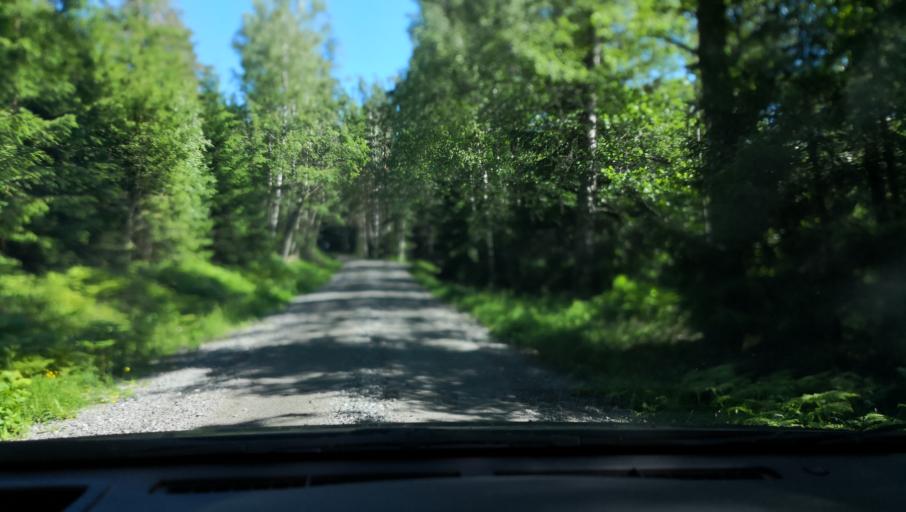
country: SE
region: Soedermanland
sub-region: Eskilstuna Kommun
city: Eskilstuna
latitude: 59.3300
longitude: 16.5815
